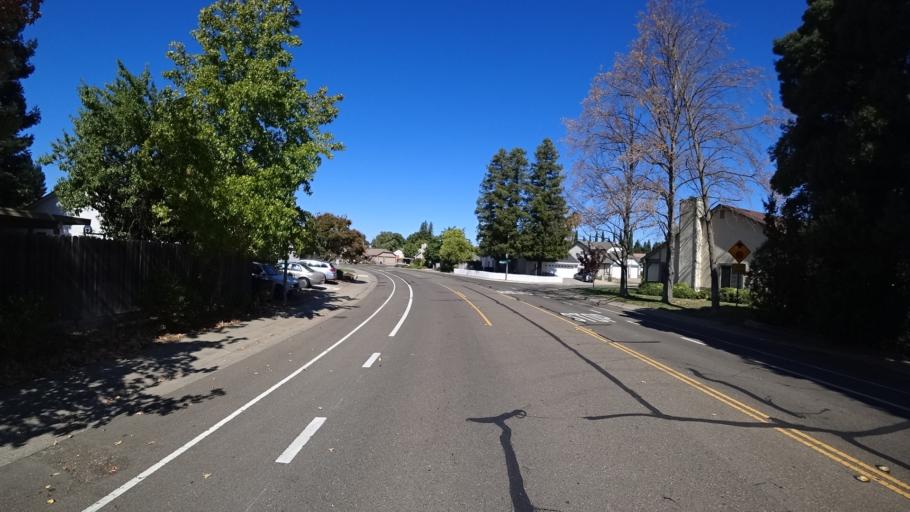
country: US
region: California
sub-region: Sacramento County
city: Elk Grove
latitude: 38.4189
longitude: -121.3838
